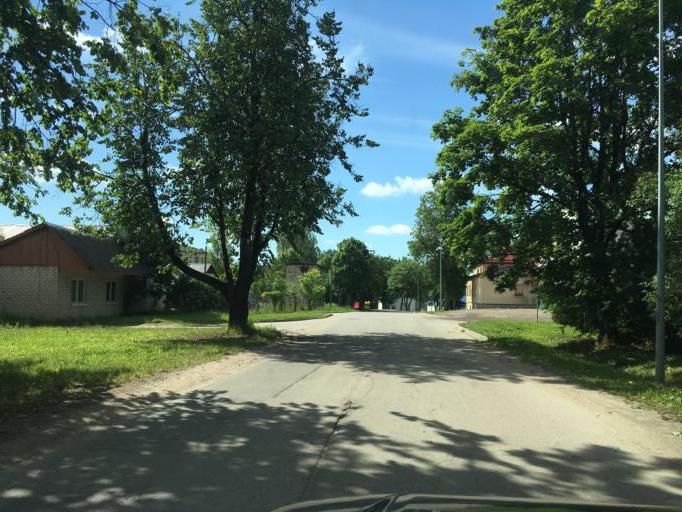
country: LV
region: Balvu Rajons
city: Balvi
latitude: 57.1406
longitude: 27.2574
